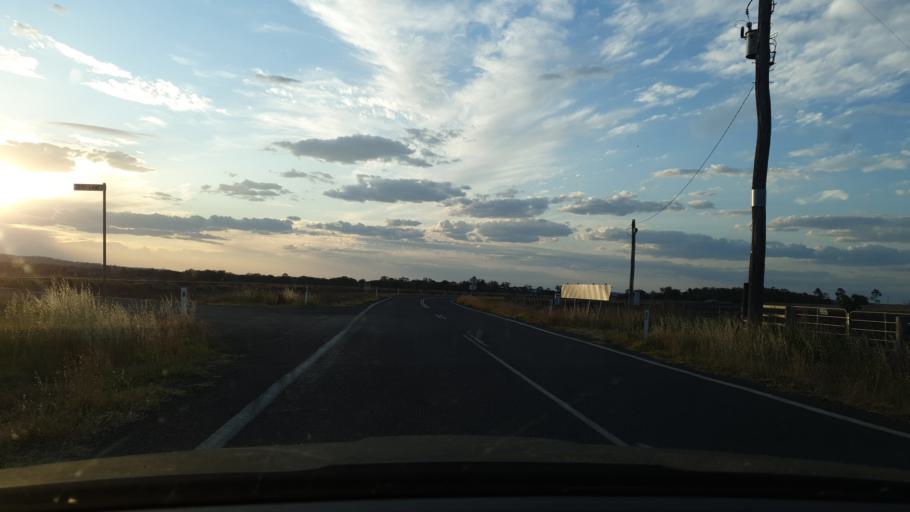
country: AU
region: Queensland
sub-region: Southern Downs
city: Warwick
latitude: -28.1821
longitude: 151.9804
